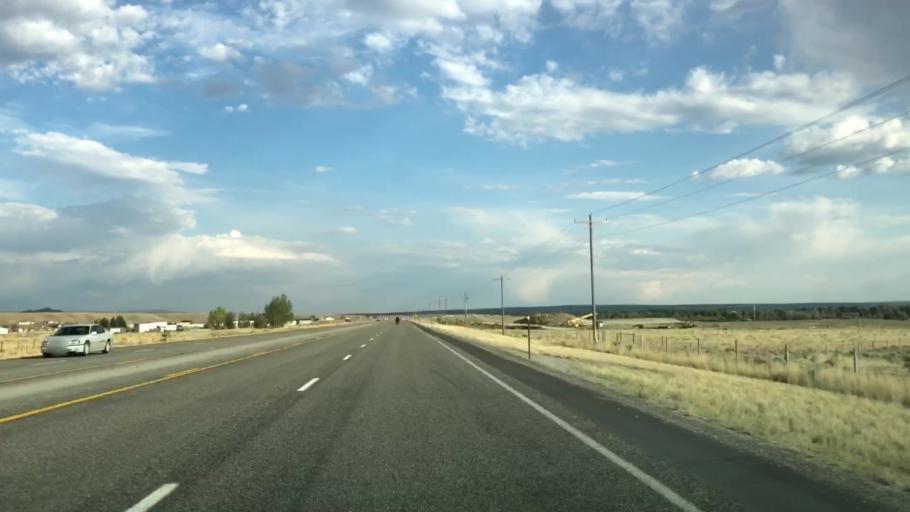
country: US
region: Wyoming
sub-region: Sublette County
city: Pinedale
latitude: 42.7742
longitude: -109.7566
